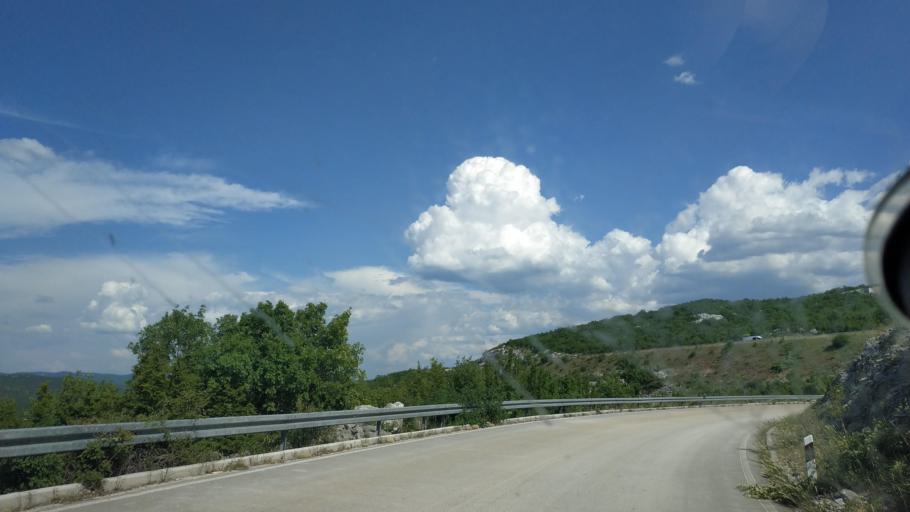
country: HR
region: Splitsko-Dalmatinska
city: Dugopolje
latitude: 43.5839
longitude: 16.6530
